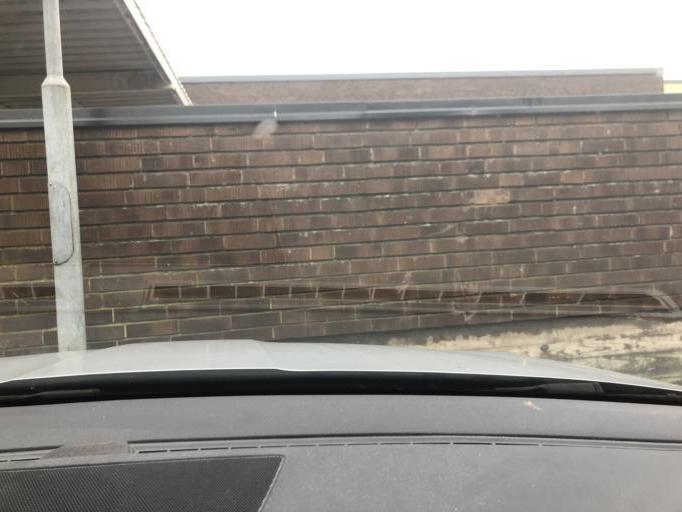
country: SE
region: Stockholm
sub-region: Botkyrka Kommun
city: Alby
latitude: 59.2379
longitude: 17.8467
